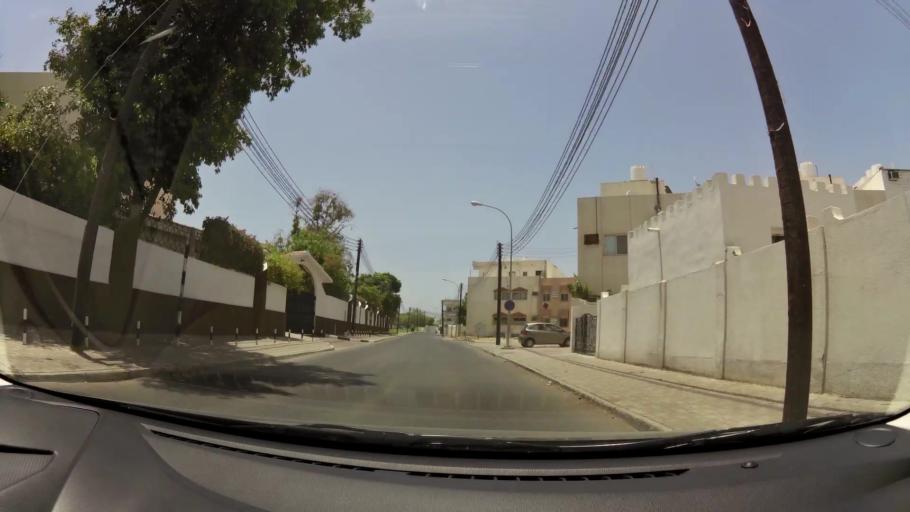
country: OM
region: Muhafazat Masqat
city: Muscat
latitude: 23.6203
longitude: 58.4952
